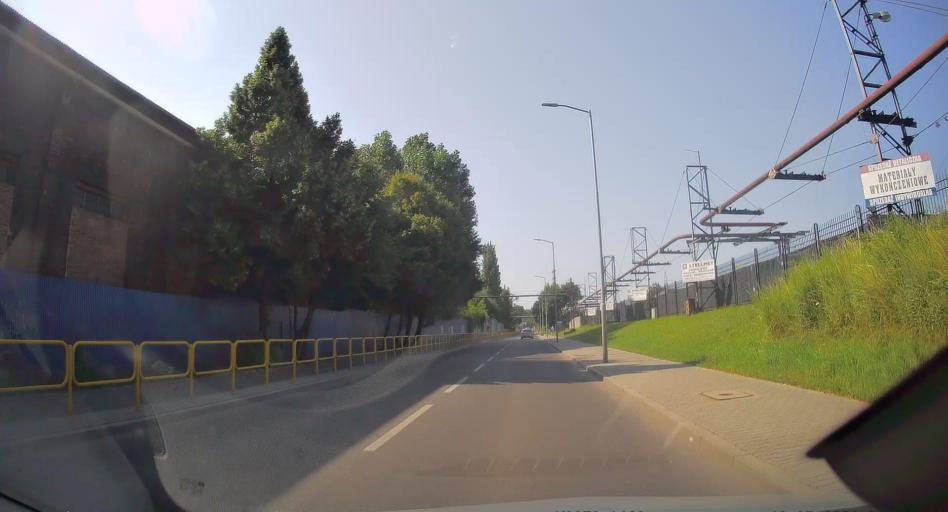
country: PL
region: Silesian Voivodeship
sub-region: Swietochlowice
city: Swietochlowice
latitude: 50.2870
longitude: 18.9139
